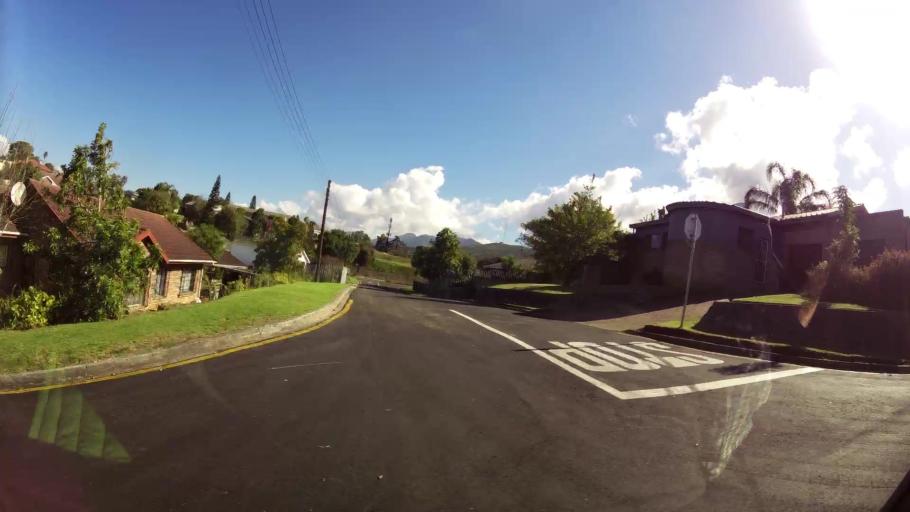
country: ZA
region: Western Cape
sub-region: Eden District Municipality
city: George
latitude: -33.9459
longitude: 22.4771
